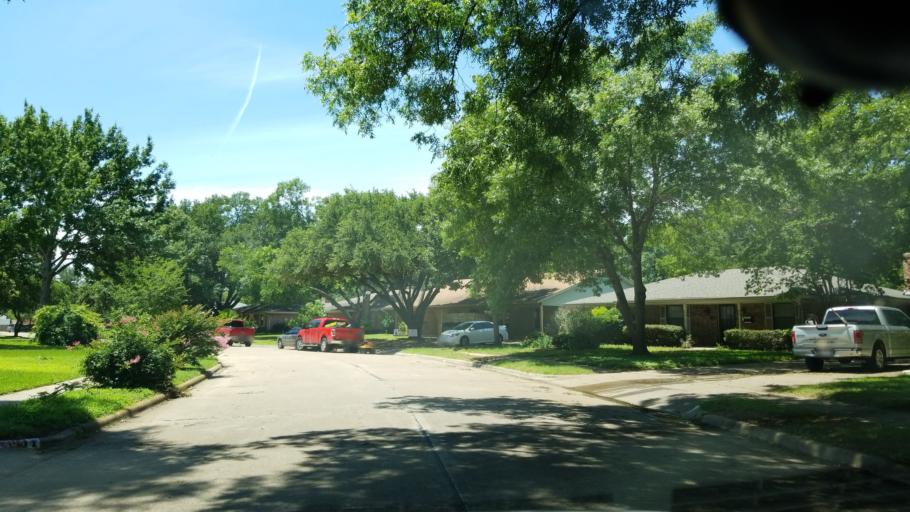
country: US
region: Texas
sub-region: Dallas County
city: Irving
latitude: 32.8215
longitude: -96.9279
